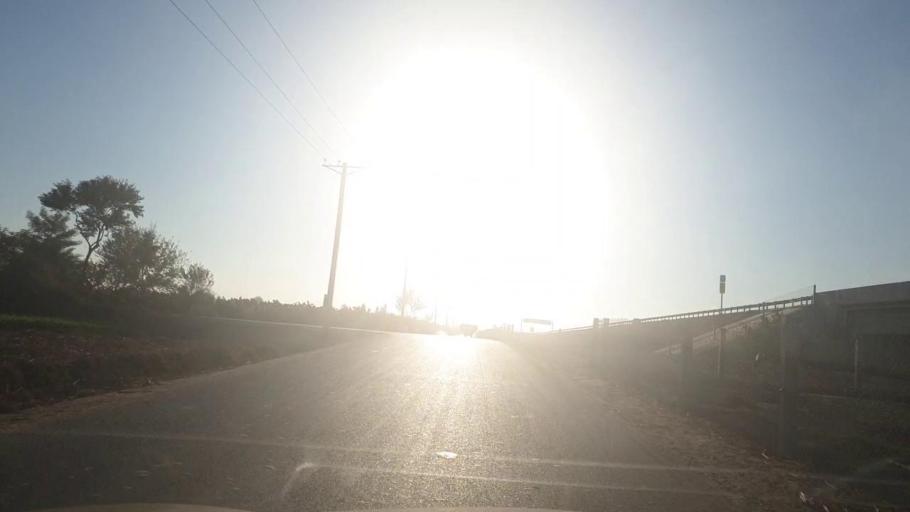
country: PK
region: Sindh
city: Ghotki
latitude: 28.0077
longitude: 69.2698
